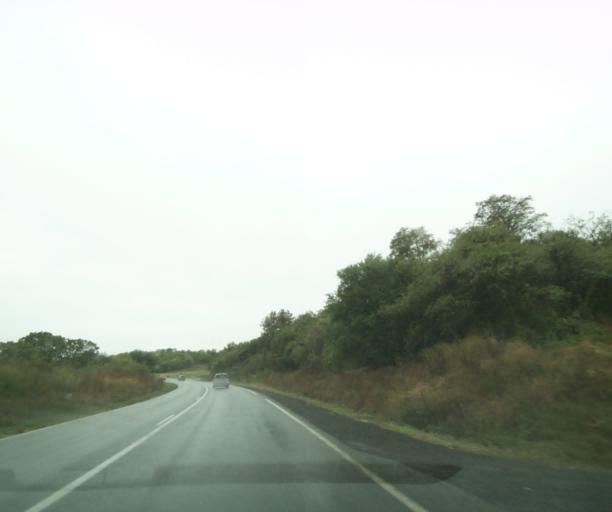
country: FR
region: Auvergne
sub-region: Departement du Puy-de-Dome
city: Cebazat
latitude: 45.8443
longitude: 3.1066
